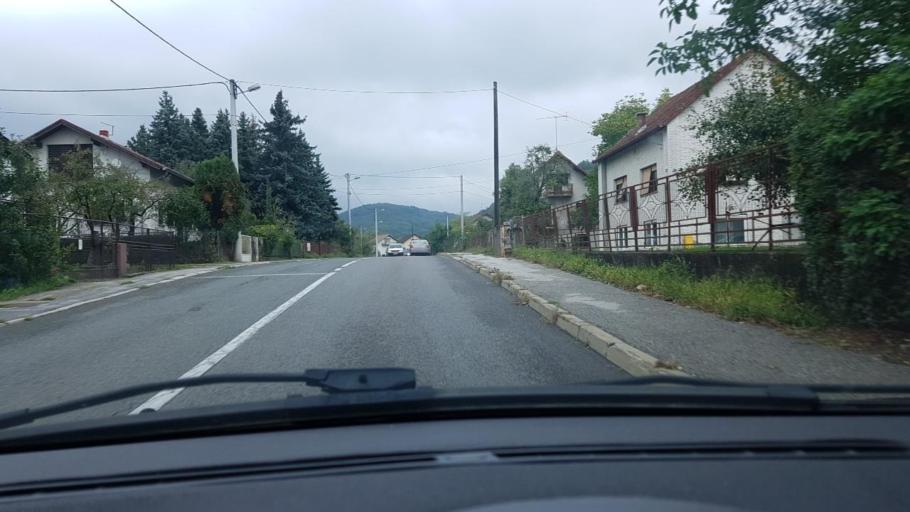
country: HR
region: Grad Zagreb
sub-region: Sesvete
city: Sesvete
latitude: 45.9128
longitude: 16.1245
